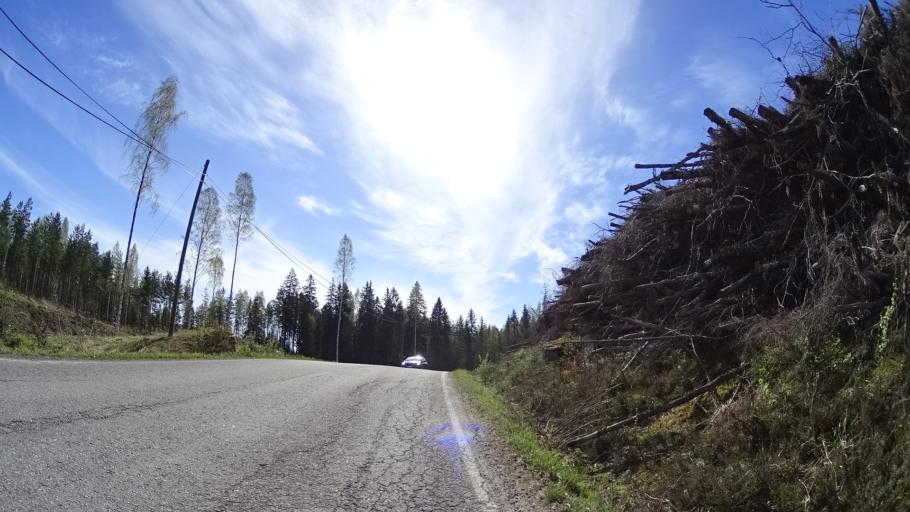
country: FI
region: Uusimaa
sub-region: Helsinki
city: Nurmijaervi
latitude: 60.4435
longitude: 24.8292
